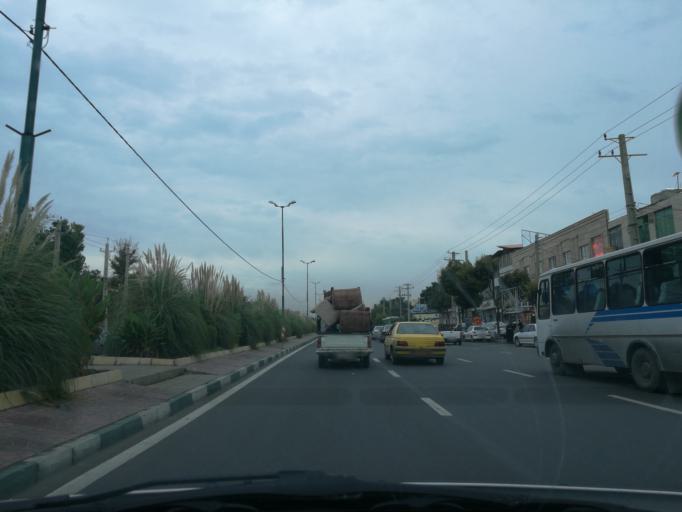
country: IR
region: Alborz
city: Karaj
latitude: 35.8458
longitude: 50.9187
